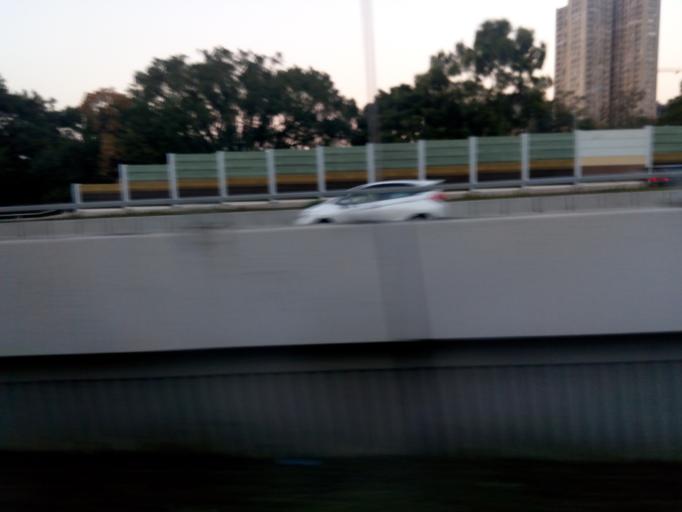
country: HK
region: Tai Po
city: Tai Po
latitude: 22.5007
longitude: 114.1220
